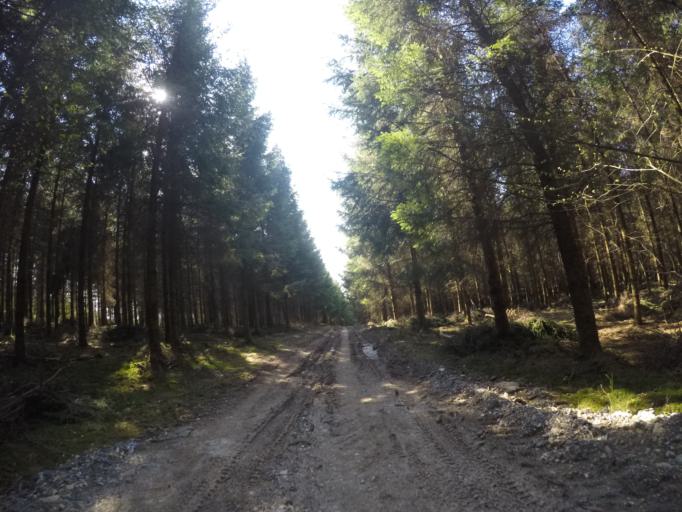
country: BE
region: Wallonia
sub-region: Province du Luxembourg
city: Leglise
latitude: 49.7851
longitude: 5.5800
